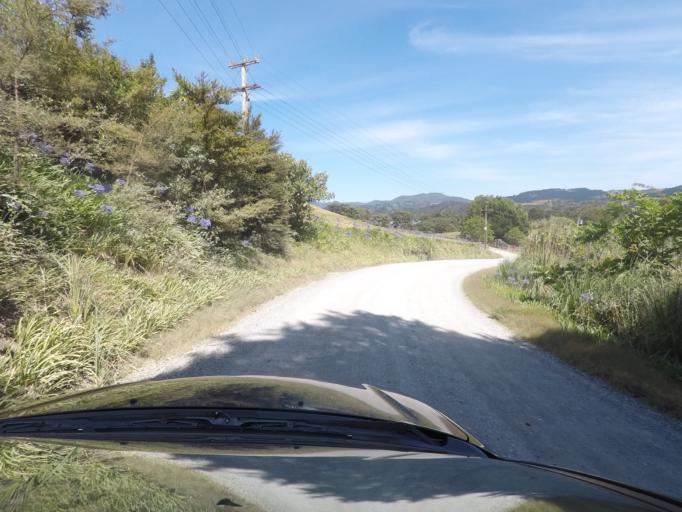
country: NZ
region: Auckland
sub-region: Auckland
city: Warkworth
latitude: -36.3171
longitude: 174.7886
